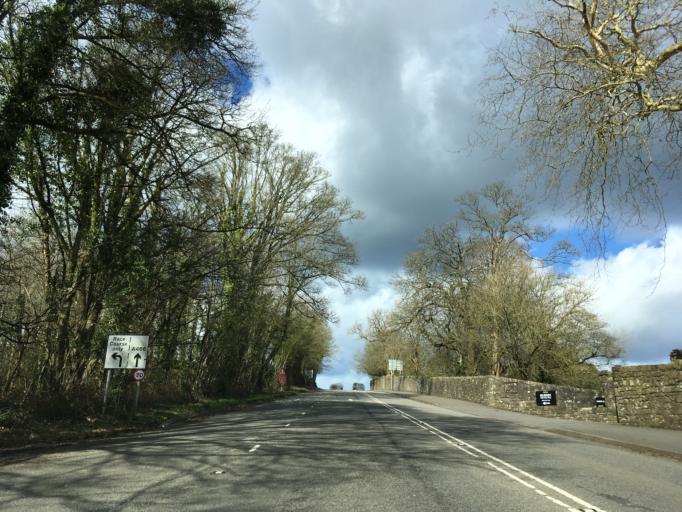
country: GB
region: Wales
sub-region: Monmouthshire
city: Chepstow
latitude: 51.6484
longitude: -2.6907
